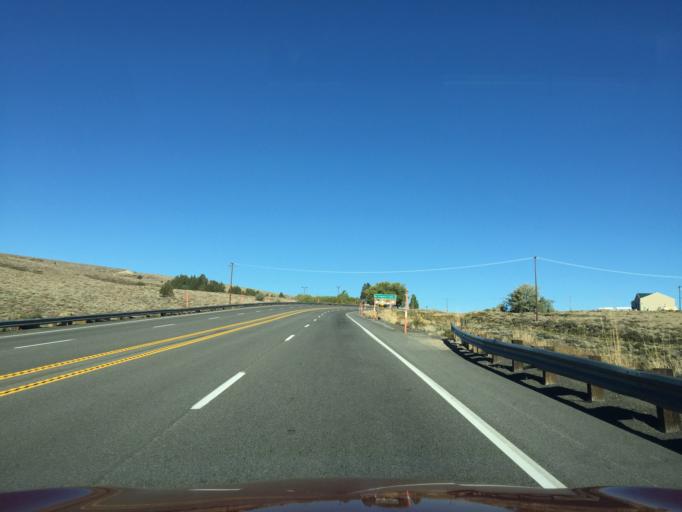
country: US
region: California
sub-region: Mono County
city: Bridgeport
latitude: 38.0850
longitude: -119.1795
